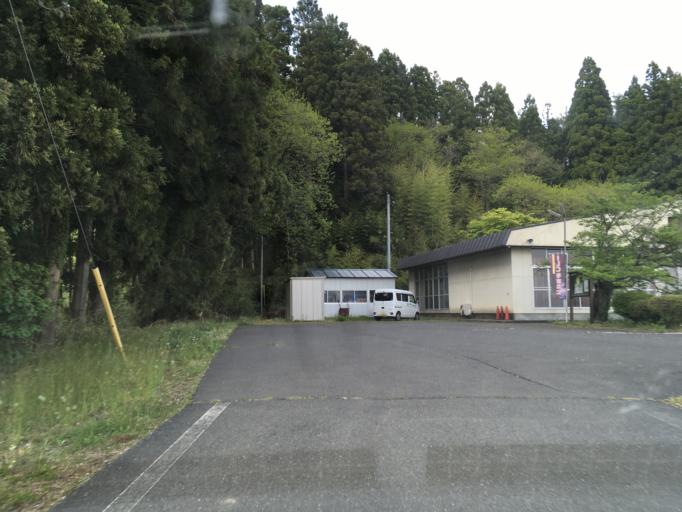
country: JP
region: Iwate
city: Ichinoseki
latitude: 38.8116
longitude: 141.1754
